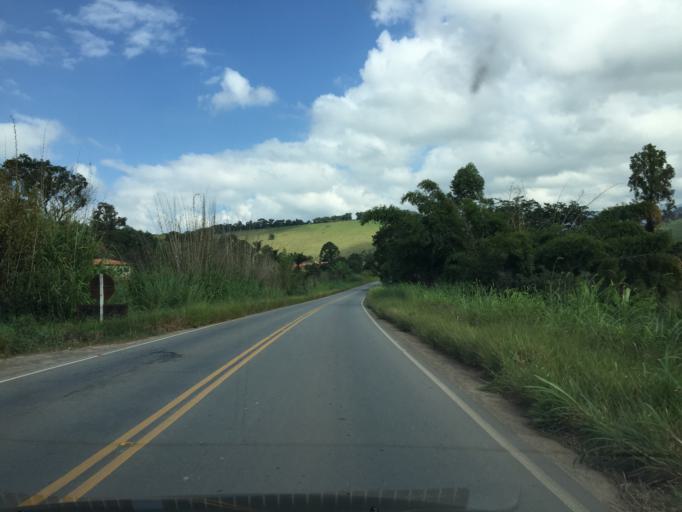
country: BR
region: Minas Gerais
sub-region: Passa Quatro
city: Passa Quatro
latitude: -22.3636
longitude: -44.9536
